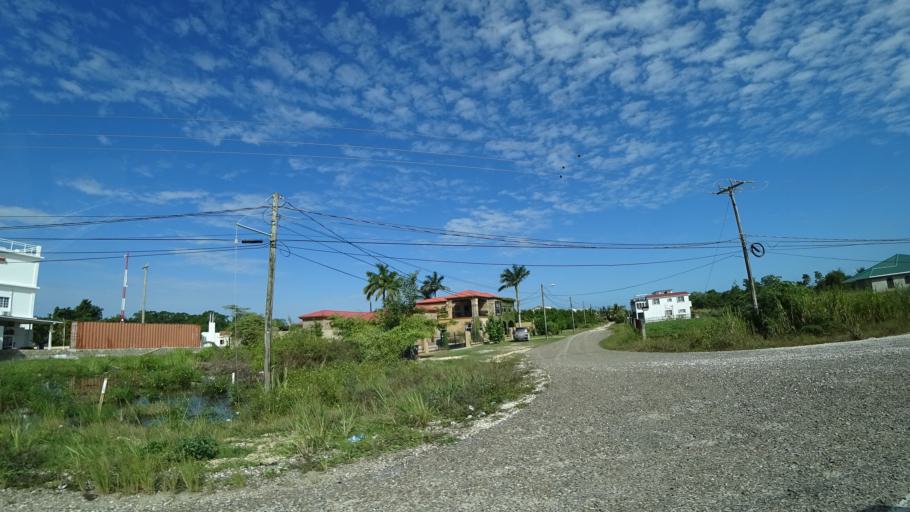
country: BZ
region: Belize
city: Belize City
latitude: 17.5447
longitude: -88.2583
